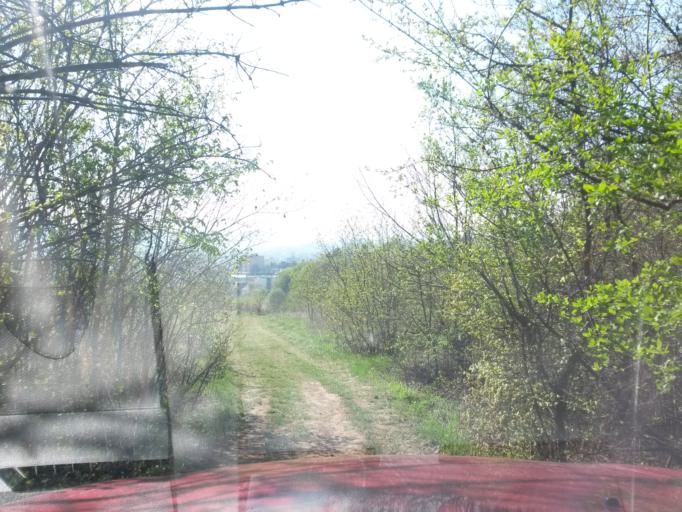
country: SK
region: Kosicky
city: Kosice
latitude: 48.7551
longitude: 21.2406
